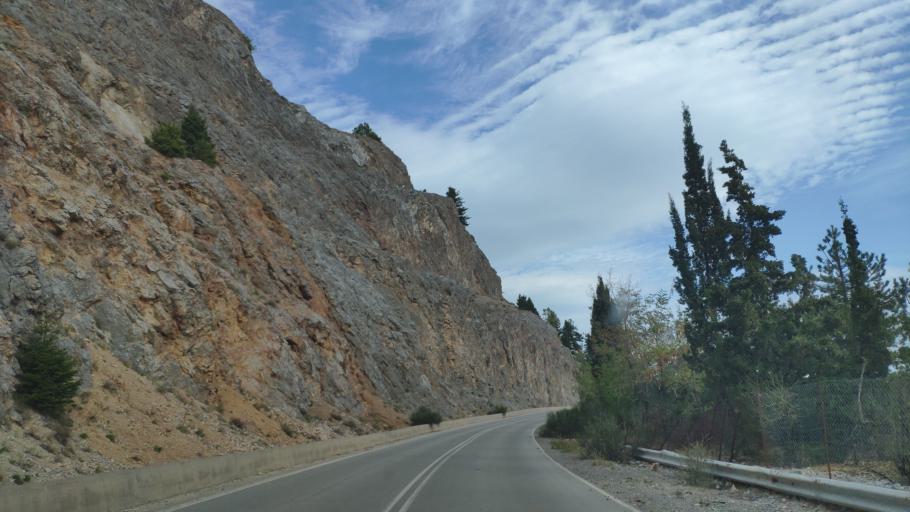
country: GR
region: Central Greece
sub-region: Nomos Fokidos
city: Amfissa
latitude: 38.6543
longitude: 22.3812
